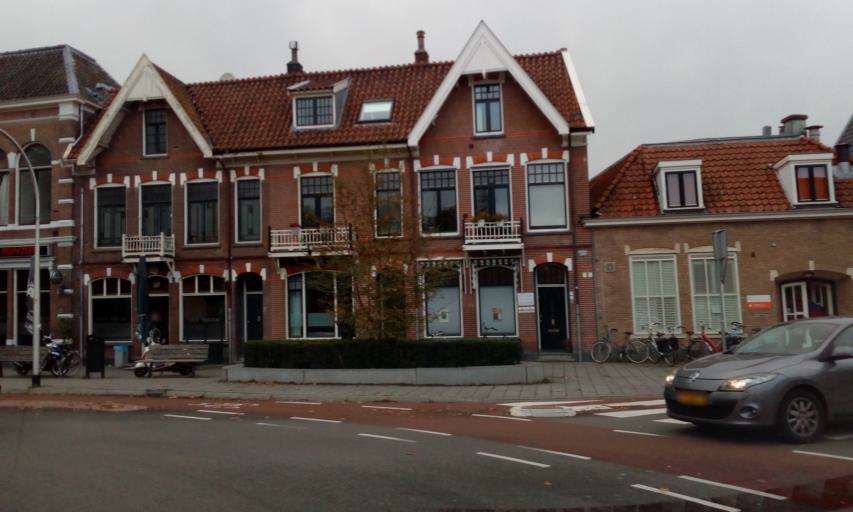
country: NL
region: Overijssel
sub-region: Gemeente Deventer
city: Deventer
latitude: 52.2582
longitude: 6.1491
